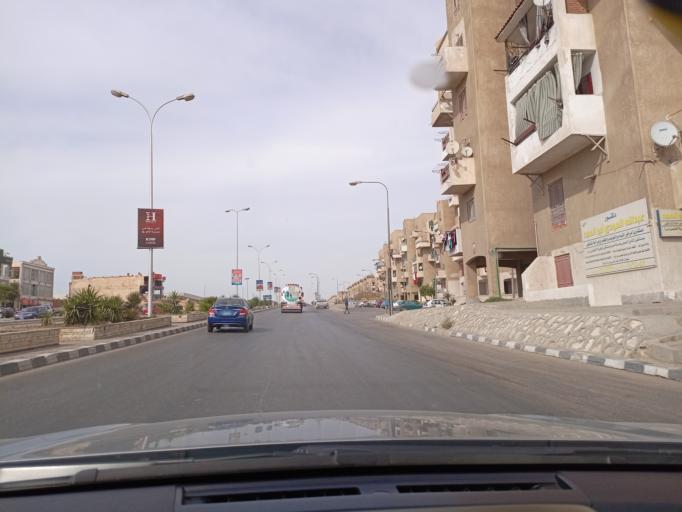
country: EG
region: Muhafazat al Qalyubiyah
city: Al Khankah
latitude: 30.2658
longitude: 31.4776
